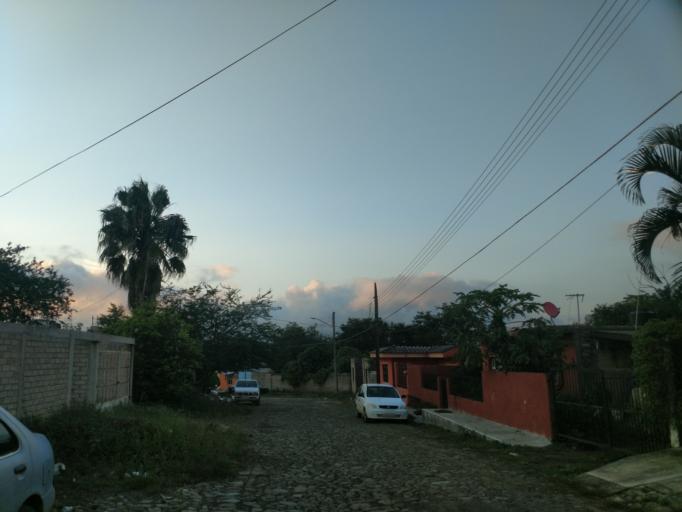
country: MX
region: Nayarit
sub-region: Tepic
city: La Corregidora
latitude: 21.4602
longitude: -104.8026
